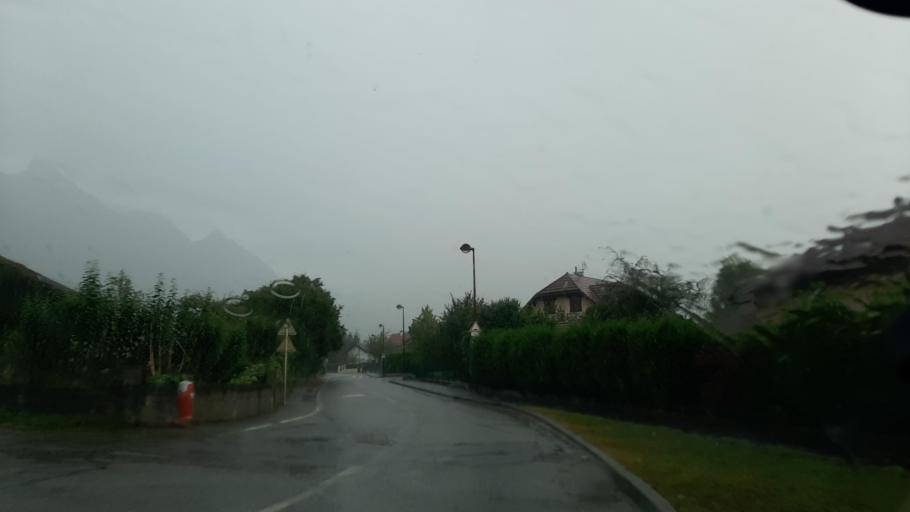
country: FR
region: Rhone-Alpes
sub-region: Departement de la Savoie
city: Gilly-sur-Isere
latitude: 45.6628
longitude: 6.3518
